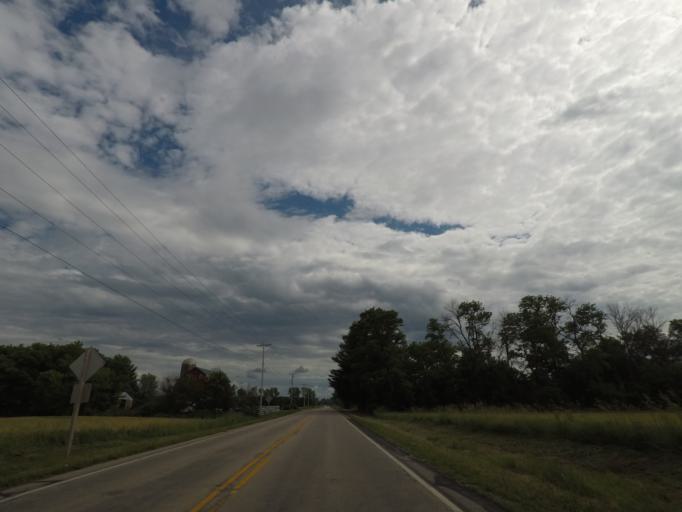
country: US
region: Wisconsin
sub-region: Dane County
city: Belleville
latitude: 42.8546
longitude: -89.5236
